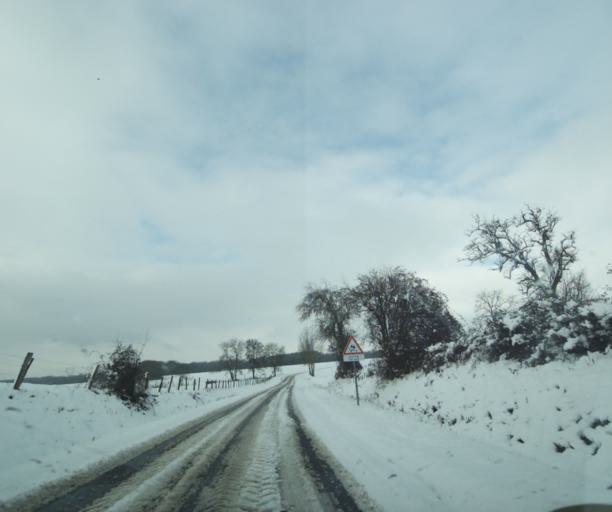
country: FR
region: Champagne-Ardenne
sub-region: Departement de la Haute-Marne
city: Montier-en-Der
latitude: 48.5121
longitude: 4.6905
